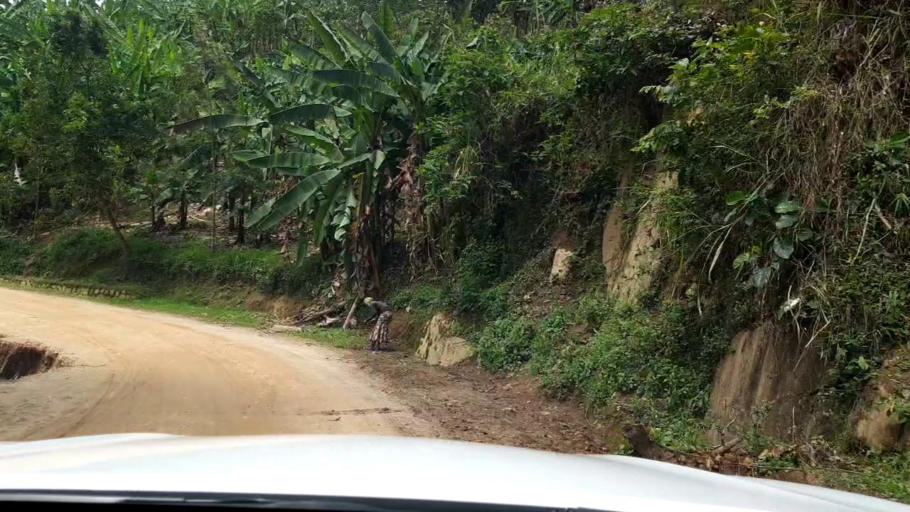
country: RW
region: Southern Province
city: Gitarama
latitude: -1.9269
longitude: 29.6514
